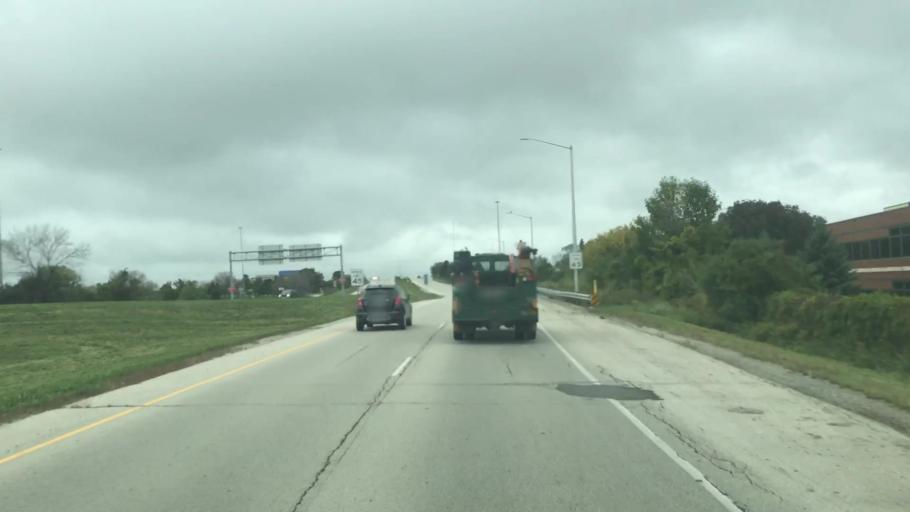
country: US
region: Wisconsin
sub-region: Waukesha County
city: Waukesha
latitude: 43.0363
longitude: -88.1692
